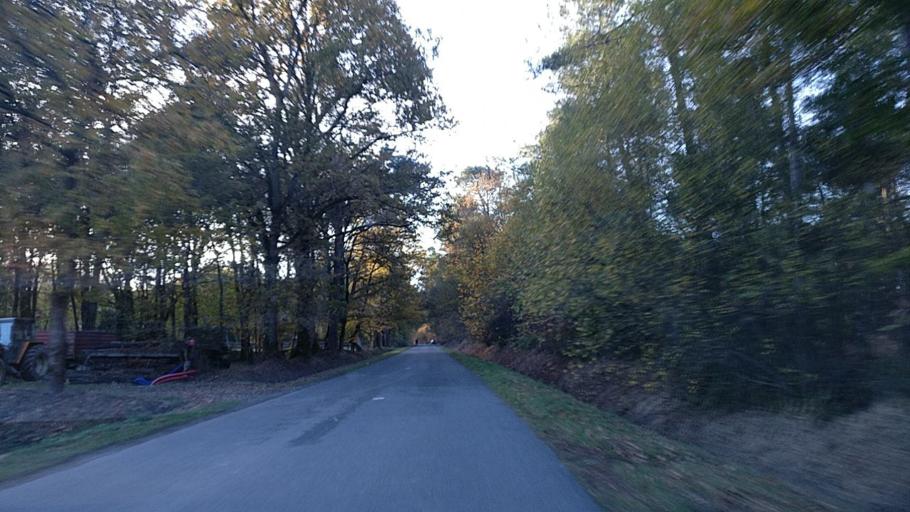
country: FR
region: Brittany
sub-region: Departement d'Ille-et-Vilaine
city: Liffre
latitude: 48.1896
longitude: -1.5278
